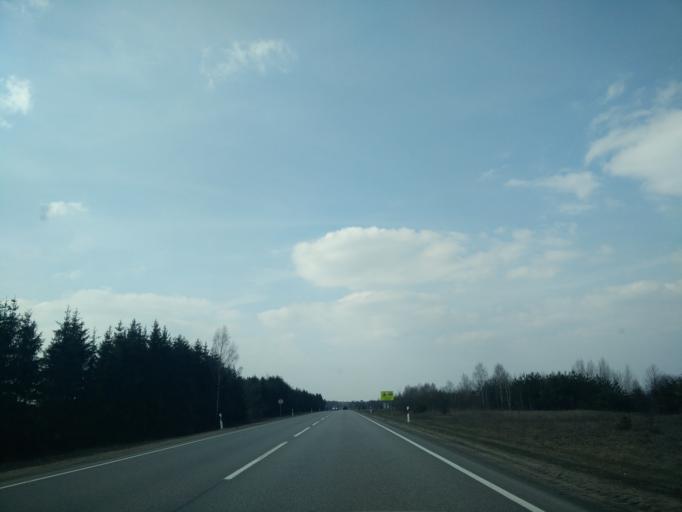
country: LT
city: Trakai
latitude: 54.6264
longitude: 24.9745
